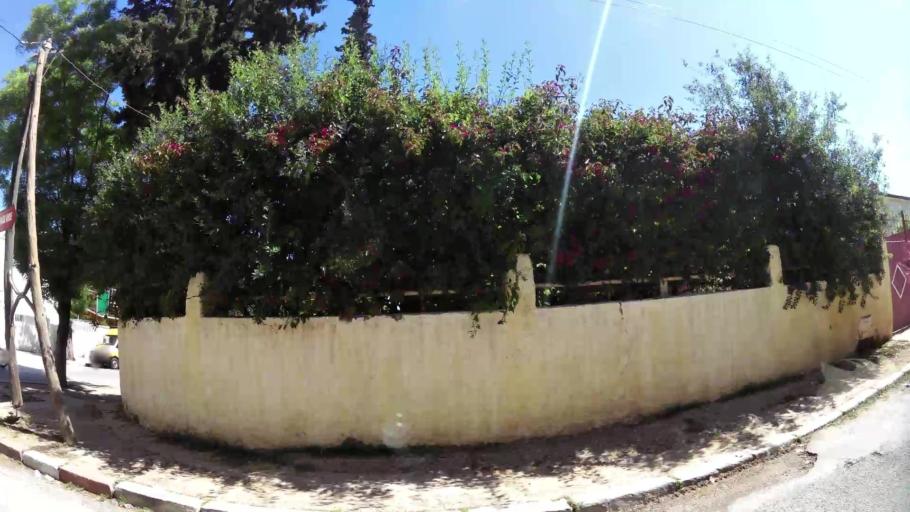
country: MA
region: Meknes-Tafilalet
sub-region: Meknes
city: Meknes
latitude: 33.9048
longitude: -5.5299
